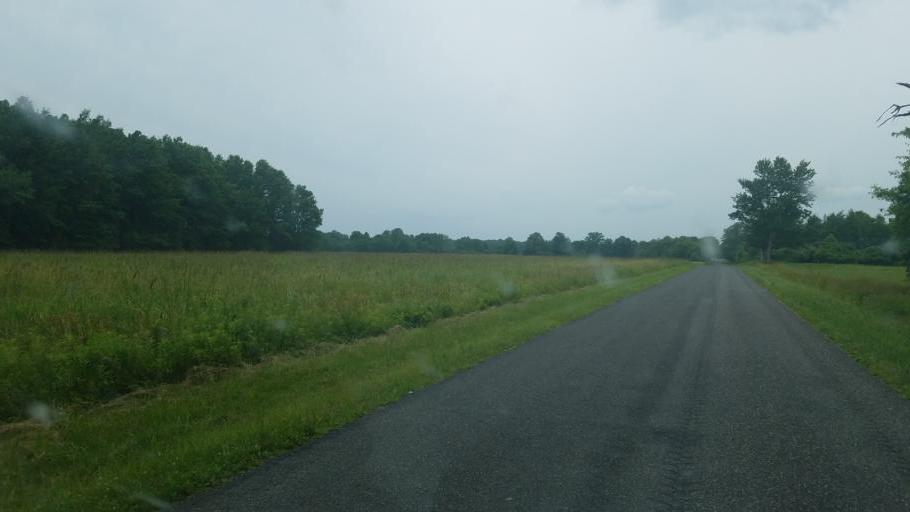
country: US
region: Ohio
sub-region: Trumbull County
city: Cortland
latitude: 41.4472
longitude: -80.7714
